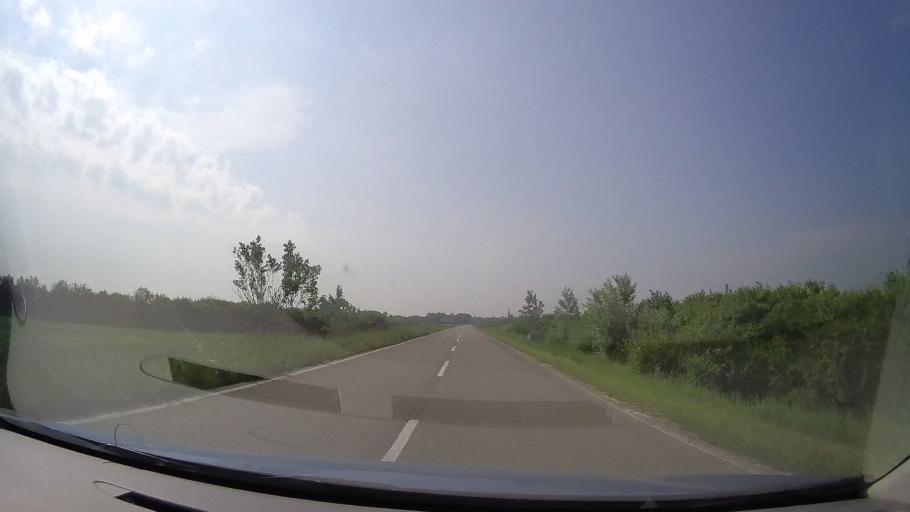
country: RS
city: Jasa Tomic
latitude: 45.4598
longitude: 20.8543
